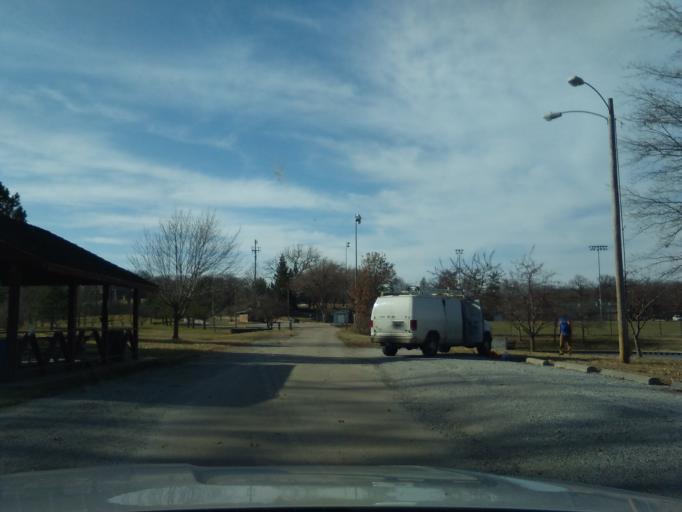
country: US
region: Nebraska
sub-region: Otoe County
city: Nebraska City
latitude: 40.6734
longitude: -95.8749
